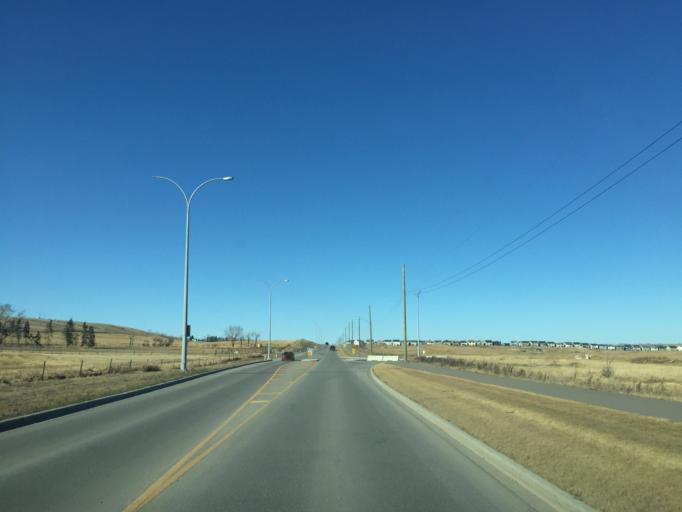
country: CA
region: Alberta
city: Airdrie
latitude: 51.2783
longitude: -114.0485
